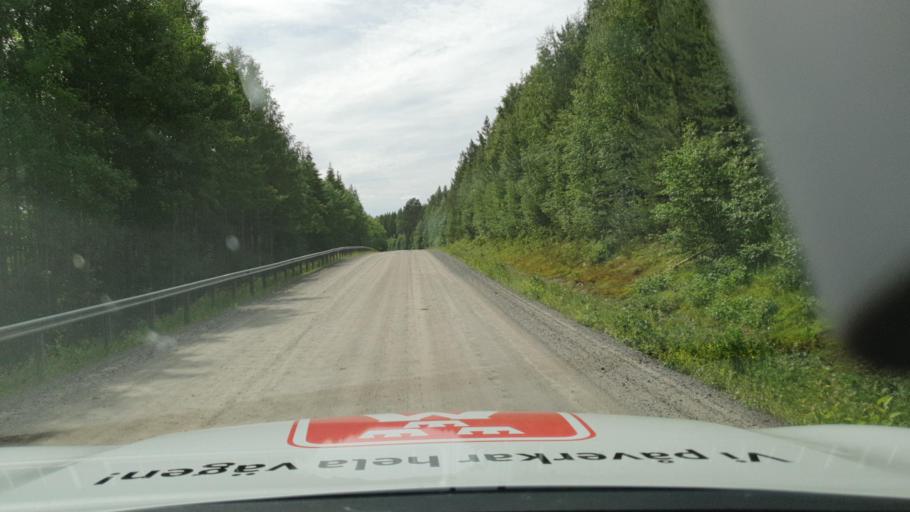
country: SE
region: Vaesterbotten
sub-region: Skelleftea Kommun
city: Burtraesk
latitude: 64.3688
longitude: 20.4155
